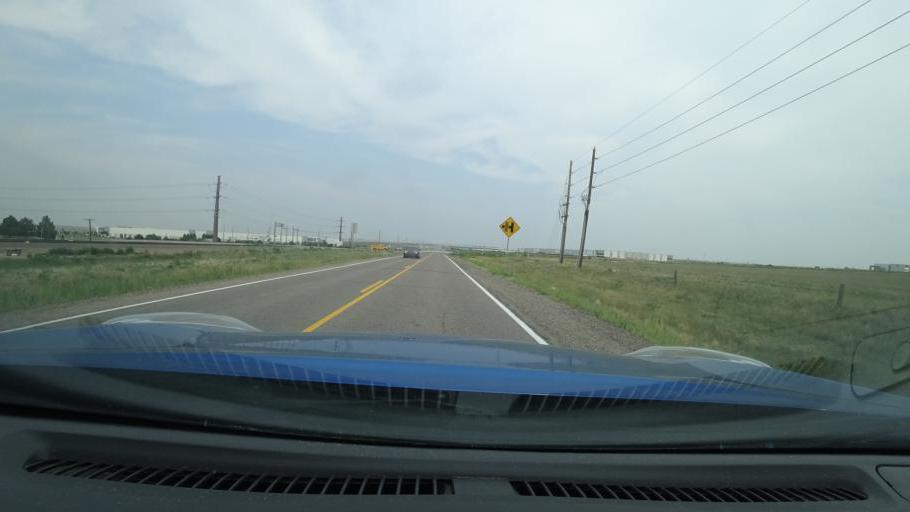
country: US
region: Colorado
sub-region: Adams County
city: Aurora
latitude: 39.7505
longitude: -104.7363
